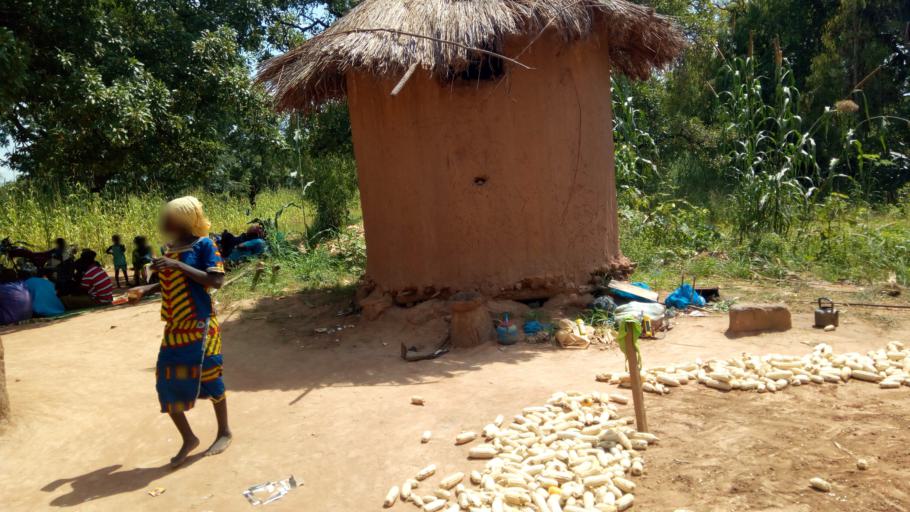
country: ML
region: Sikasso
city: Yorosso
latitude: 12.1992
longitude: -4.9159
